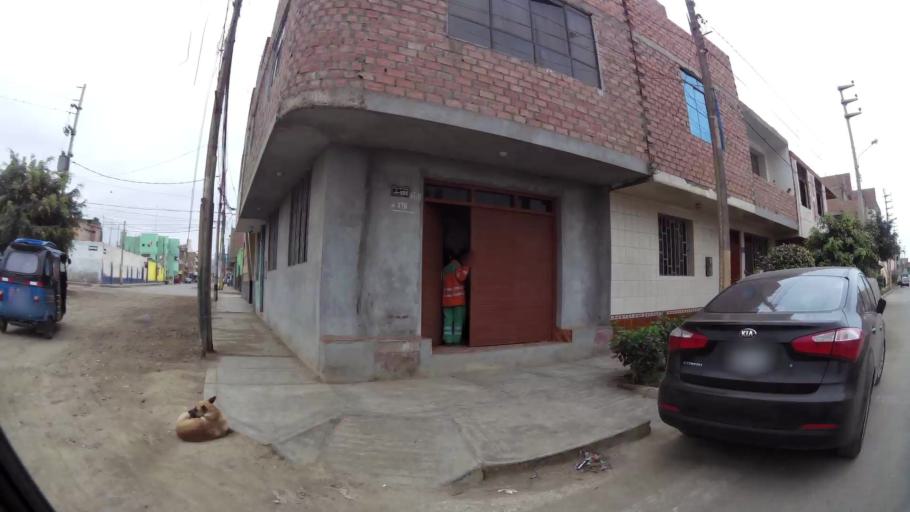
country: PE
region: Lima
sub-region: Barranca
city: Paramonga
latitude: -10.6736
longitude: -77.8202
